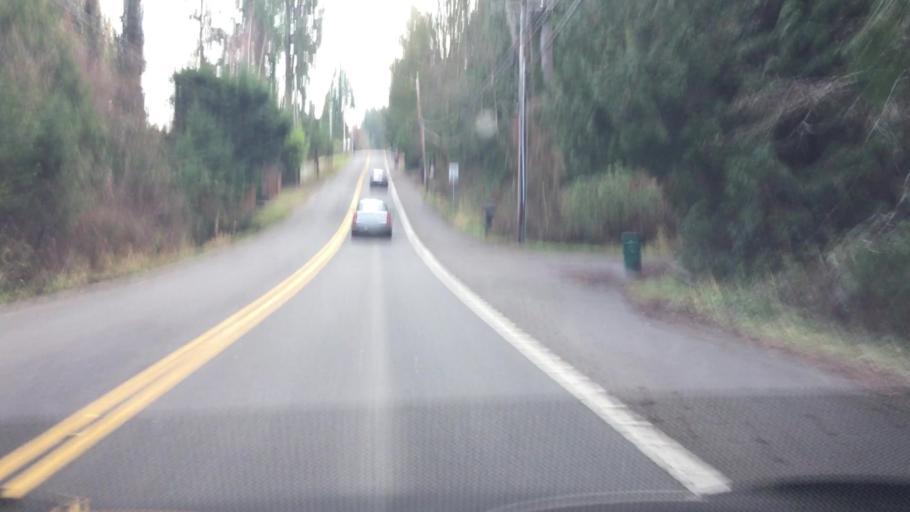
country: US
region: Washington
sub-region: King County
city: Woodinville
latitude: 47.7660
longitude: -122.1317
